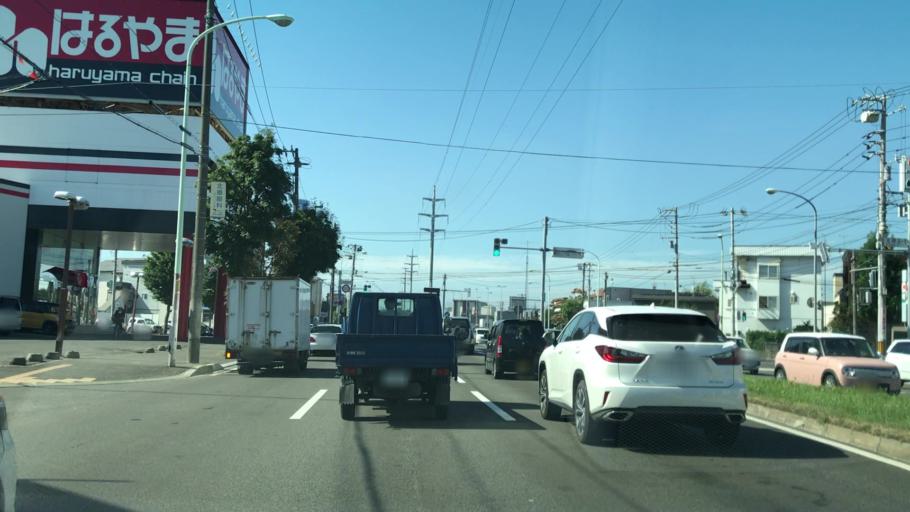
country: JP
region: Hokkaido
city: Sapporo
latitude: 43.0634
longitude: 141.4079
